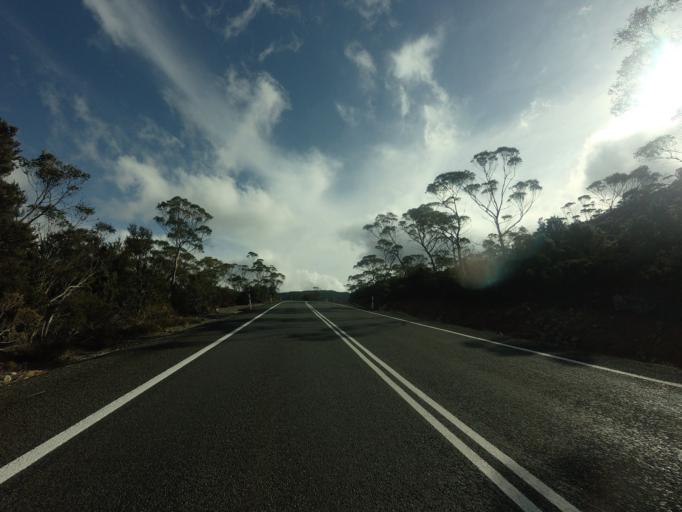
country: AU
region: Tasmania
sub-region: Meander Valley
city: Deloraine
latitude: -41.7306
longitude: 146.7142
